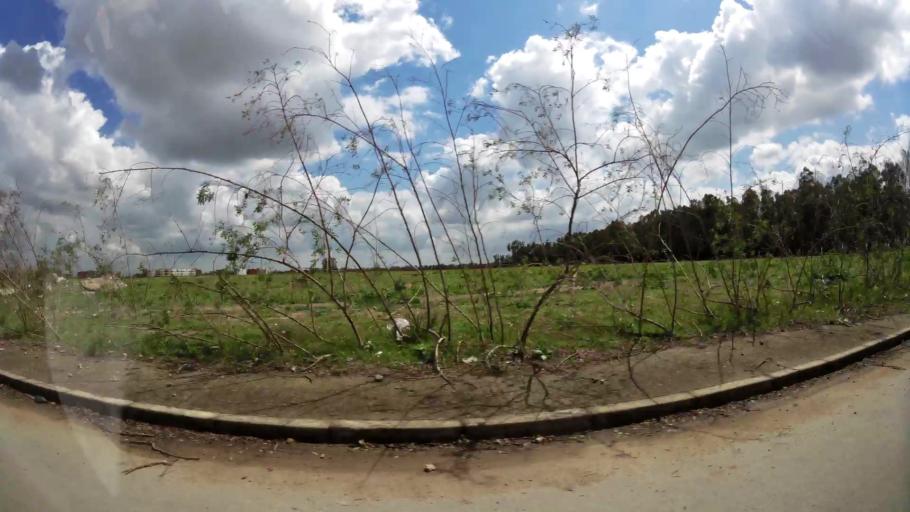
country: MA
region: Chaouia-Ouardigha
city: Nouaseur
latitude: 33.3874
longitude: -7.5534
